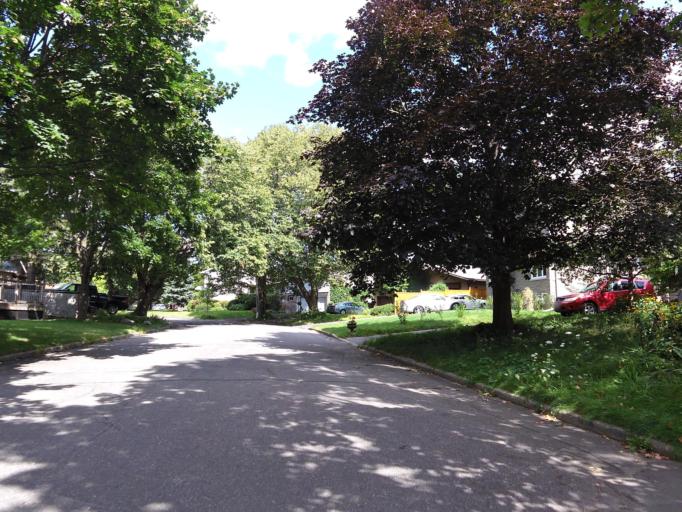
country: CA
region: Ontario
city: Bells Corners
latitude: 45.3666
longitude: -75.7666
